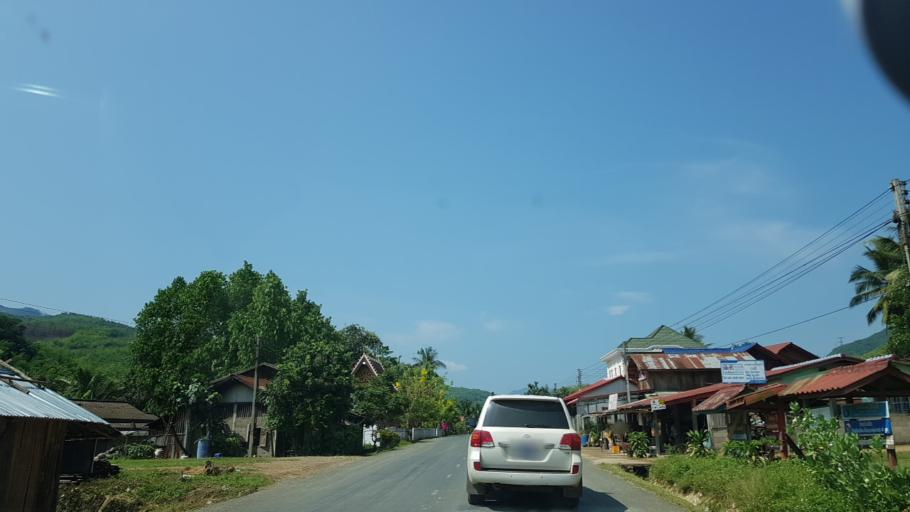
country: LA
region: Louangphabang
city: Xiang Ngeun
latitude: 19.7311
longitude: 102.1546
